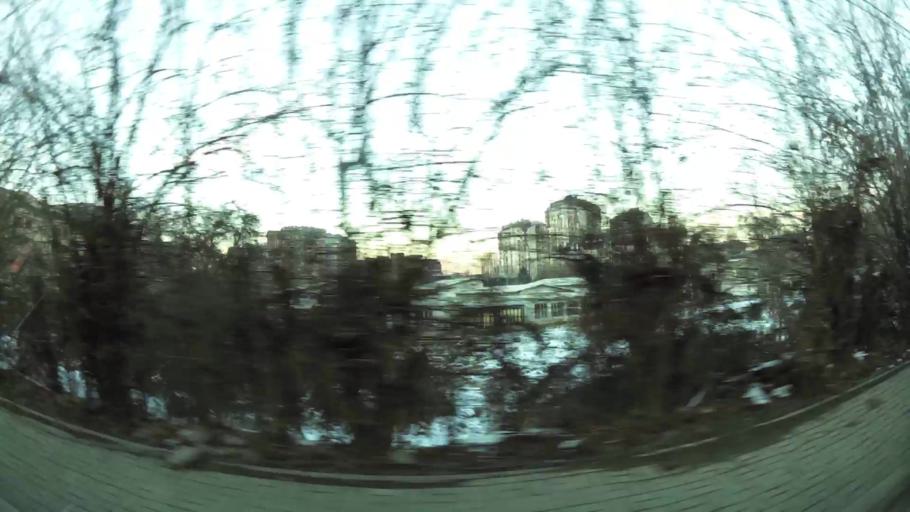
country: MK
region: Karpos
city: Skopje
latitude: 41.9914
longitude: 21.4126
